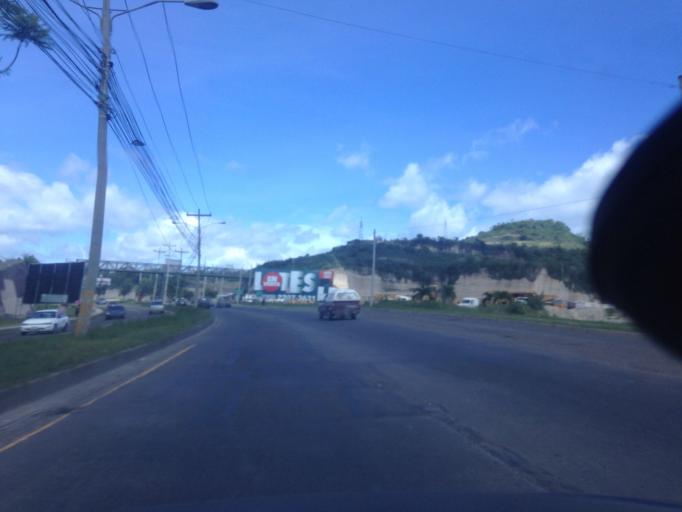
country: HN
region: Francisco Morazan
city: Tegucigalpa
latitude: 14.0491
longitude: -87.1998
